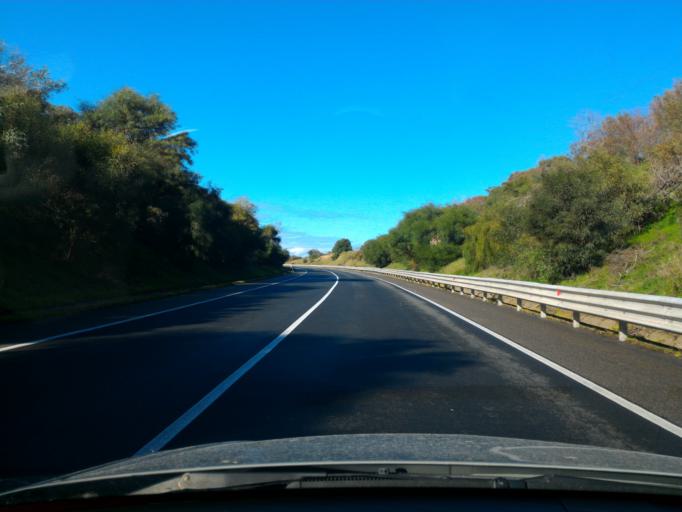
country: IT
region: Calabria
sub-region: Provincia di Crotone
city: Ciro Marina
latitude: 39.3940
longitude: 17.1216
